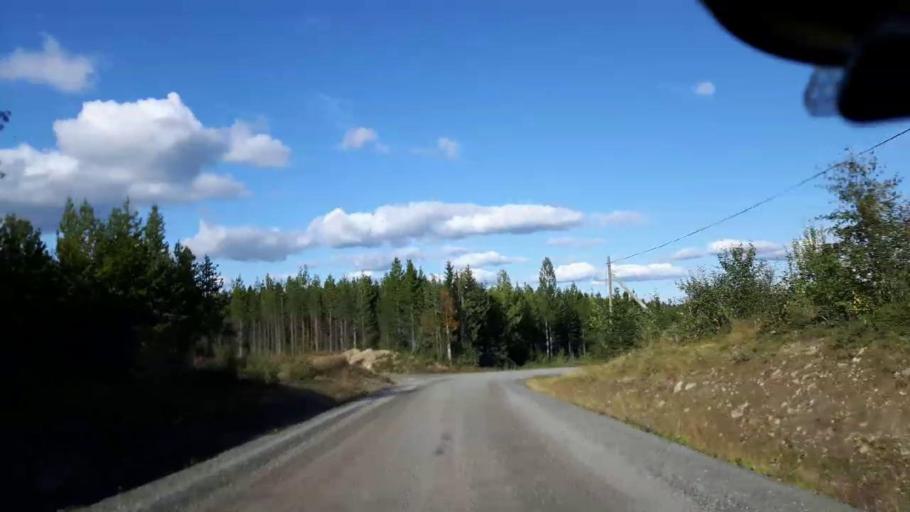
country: SE
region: Vaesternorrland
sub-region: Solleftea Kommun
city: As
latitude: 63.4529
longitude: 16.2297
